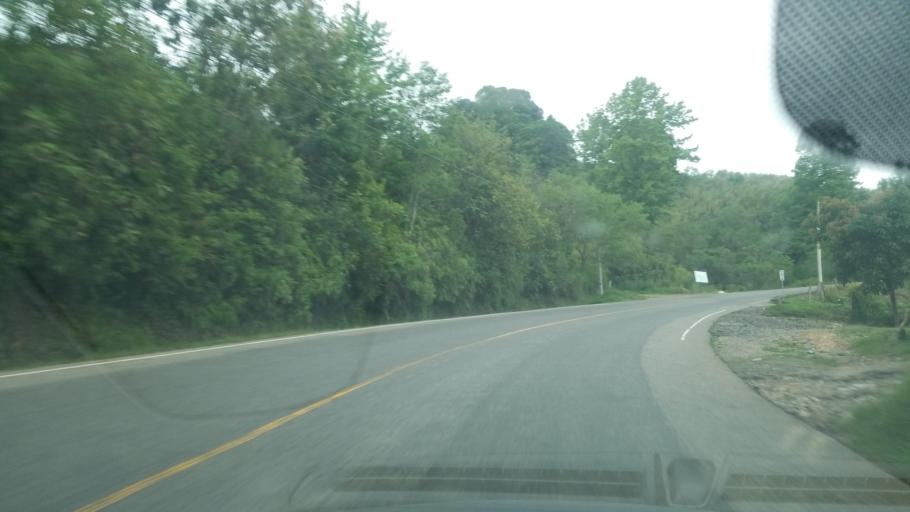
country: HN
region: Ocotepeque
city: La Labor
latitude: 14.4807
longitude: -89.0506
